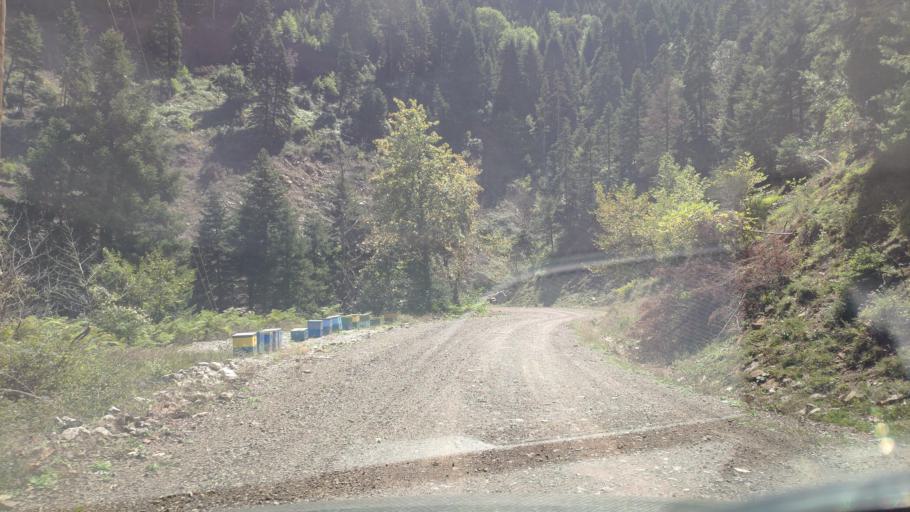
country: GR
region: Central Greece
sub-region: Nomos Evrytanias
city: Kerasochori
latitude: 39.1136
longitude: 21.6221
